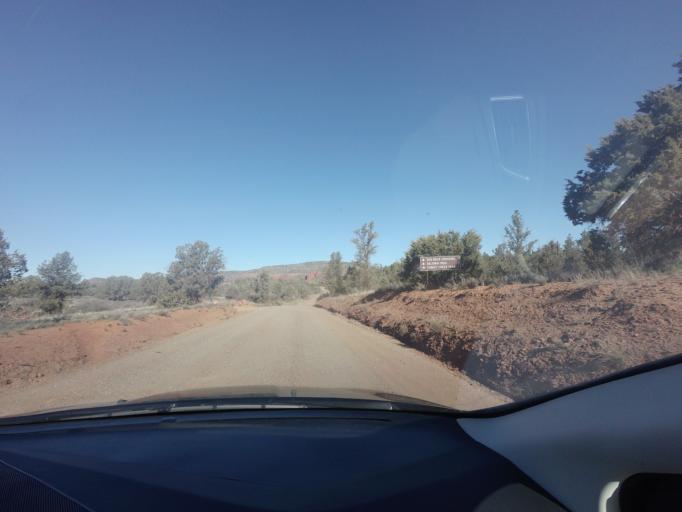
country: US
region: Arizona
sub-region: Yavapai County
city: West Sedona
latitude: 34.8128
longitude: -111.8092
